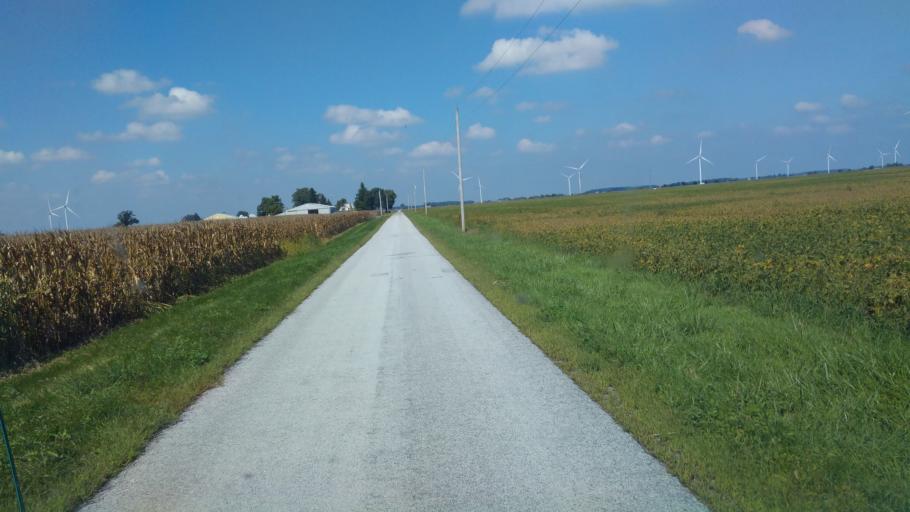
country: US
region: Ohio
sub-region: Hardin County
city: Ada
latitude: 40.7634
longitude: -83.7479
